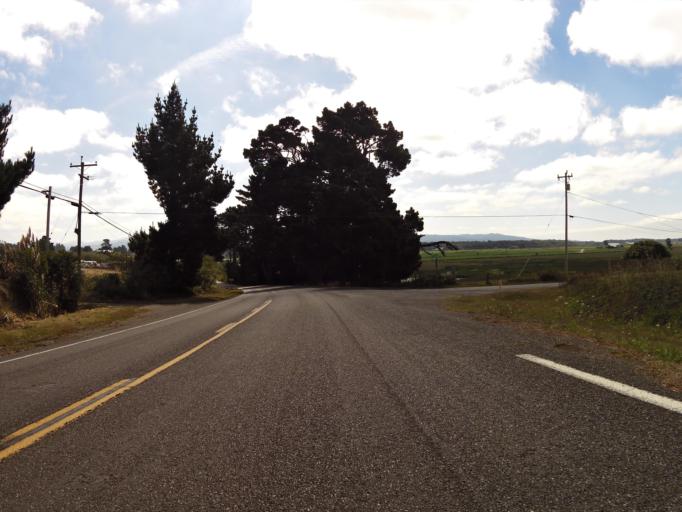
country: US
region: California
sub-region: Humboldt County
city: Ferndale
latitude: 40.6469
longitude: -124.2261
